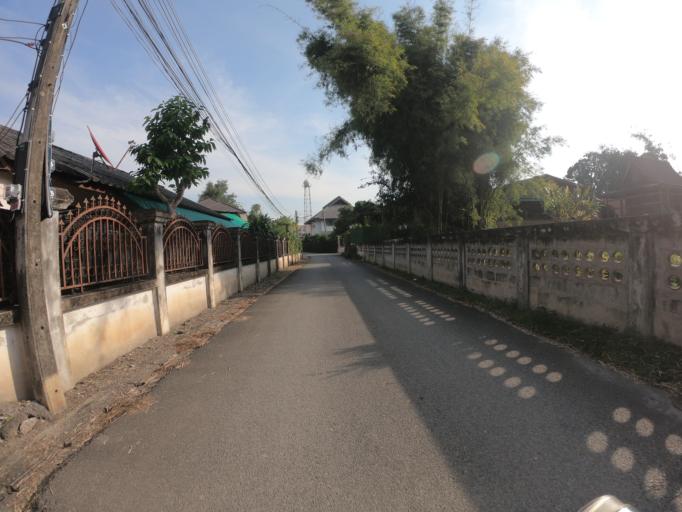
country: TH
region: Chiang Mai
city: Chiang Mai
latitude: 18.8341
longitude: 98.9945
